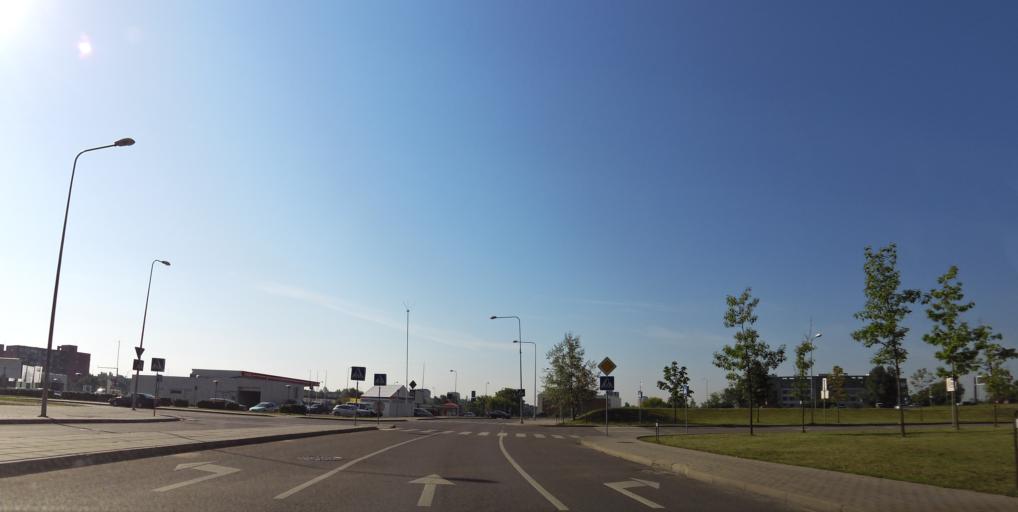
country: LT
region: Vilnius County
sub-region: Vilnius
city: Vilnius
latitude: 54.7144
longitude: 25.2761
